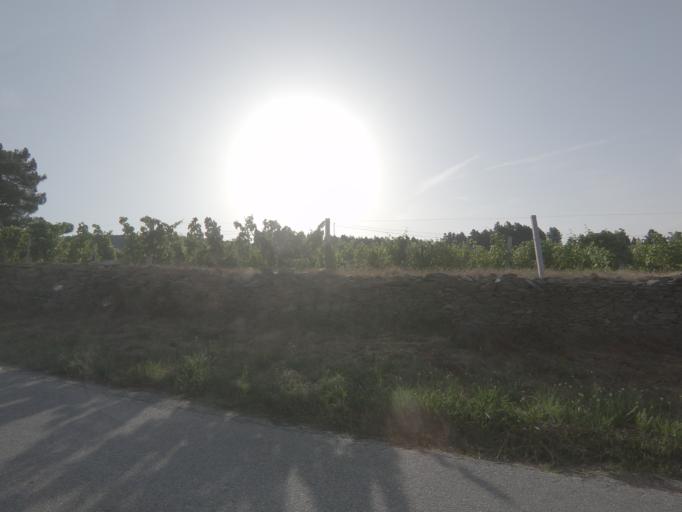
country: PT
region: Vila Real
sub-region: Sabrosa
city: Sabrosa
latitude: 41.2470
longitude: -7.4671
